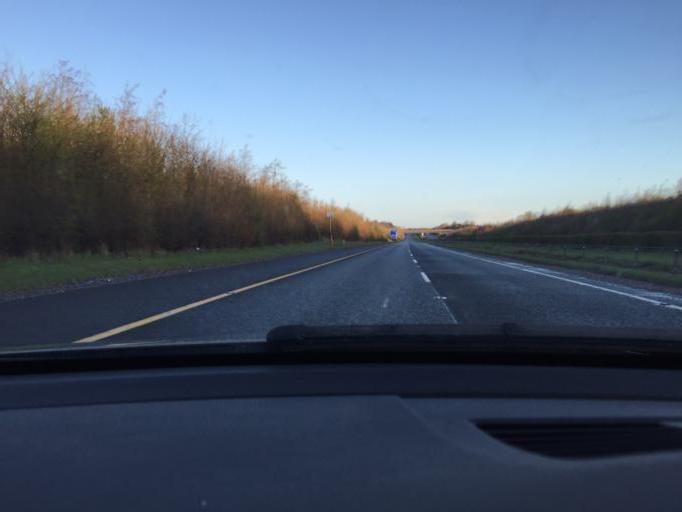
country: IE
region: Leinster
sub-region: Lu
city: Drogheda
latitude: 53.6811
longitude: -6.3612
